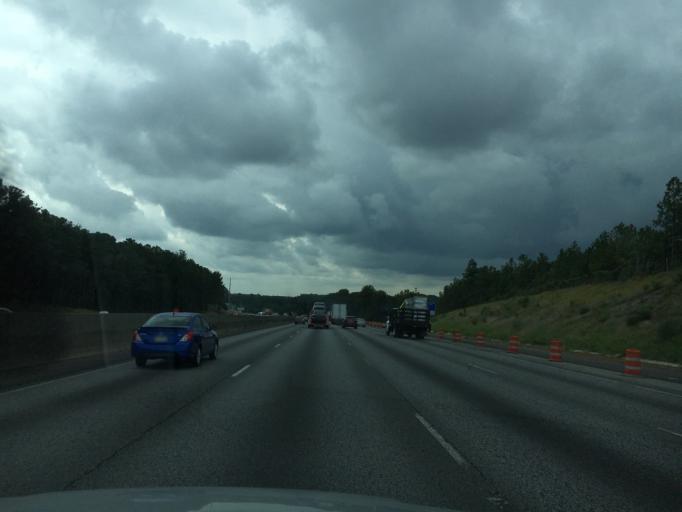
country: US
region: Georgia
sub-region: Gwinnett County
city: Suwanee
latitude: 34.0217
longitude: -84.0590
